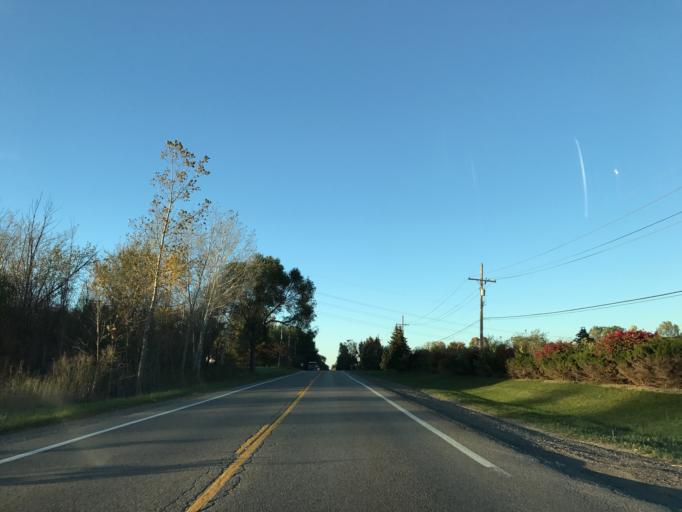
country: US
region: Michigan
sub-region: Oakland County
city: South Lyon
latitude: 42.4654
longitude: -83.6126
